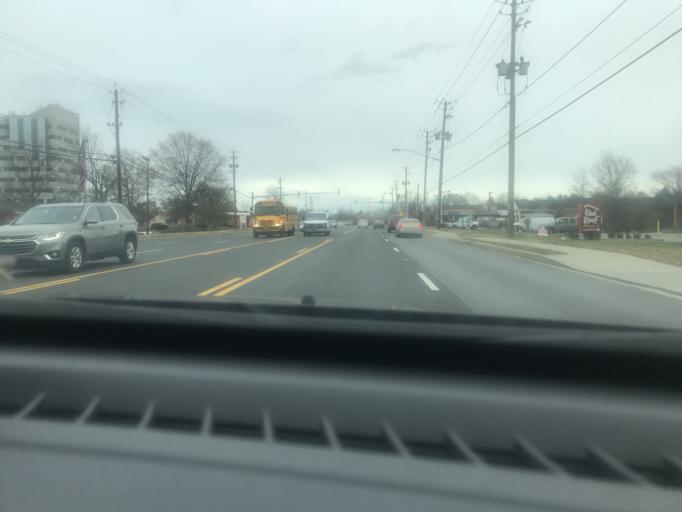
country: US
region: Maryland
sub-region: Prince George's County
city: Oxon Hill
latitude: 38.8044
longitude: -76.9807
